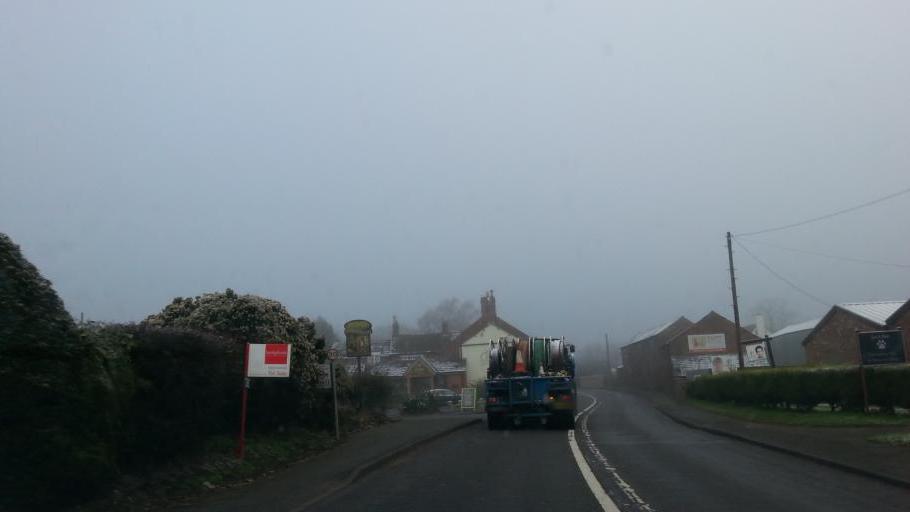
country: GB
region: England
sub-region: Cheshire East
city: Siddington
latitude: 53.2092
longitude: -2.2261
